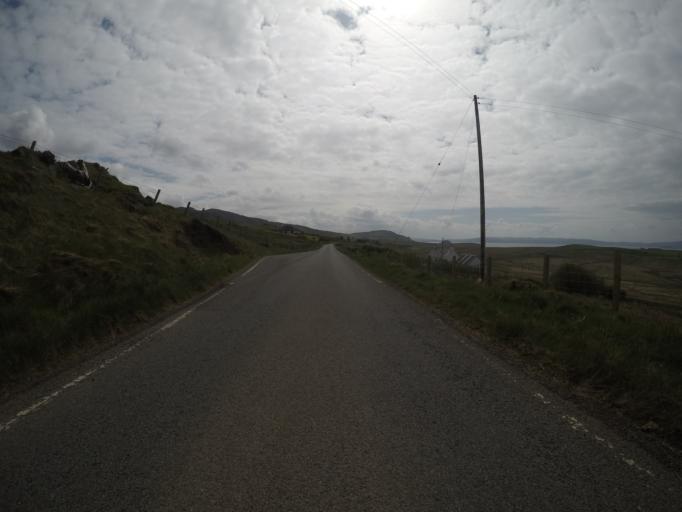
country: GB
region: Scotland
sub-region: Highland
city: Portree
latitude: 57.6259
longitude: -6.3775
